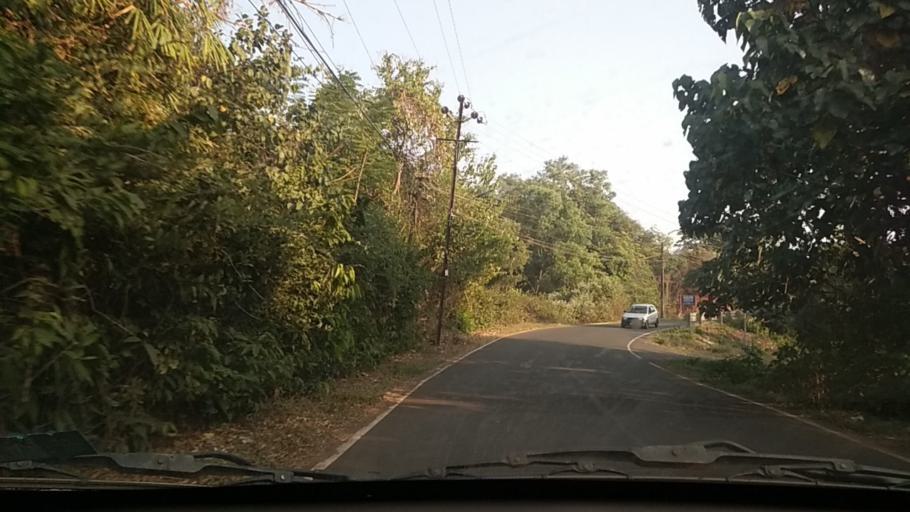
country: IN
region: Goa
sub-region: North Goa
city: Bambolim
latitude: 15.4789
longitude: 73.8625
